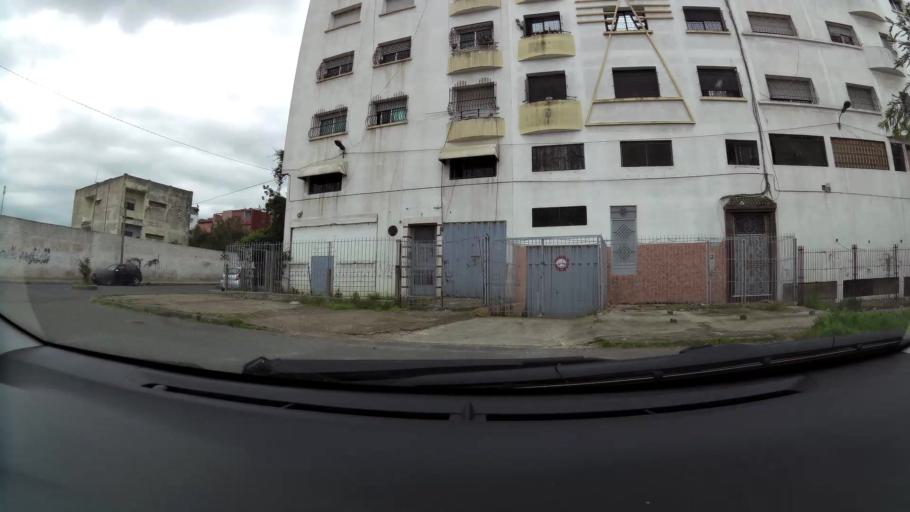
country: MA
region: Grand Casablanca
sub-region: Casablanca
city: Casablanca
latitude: 33.5577
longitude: -7.5583
